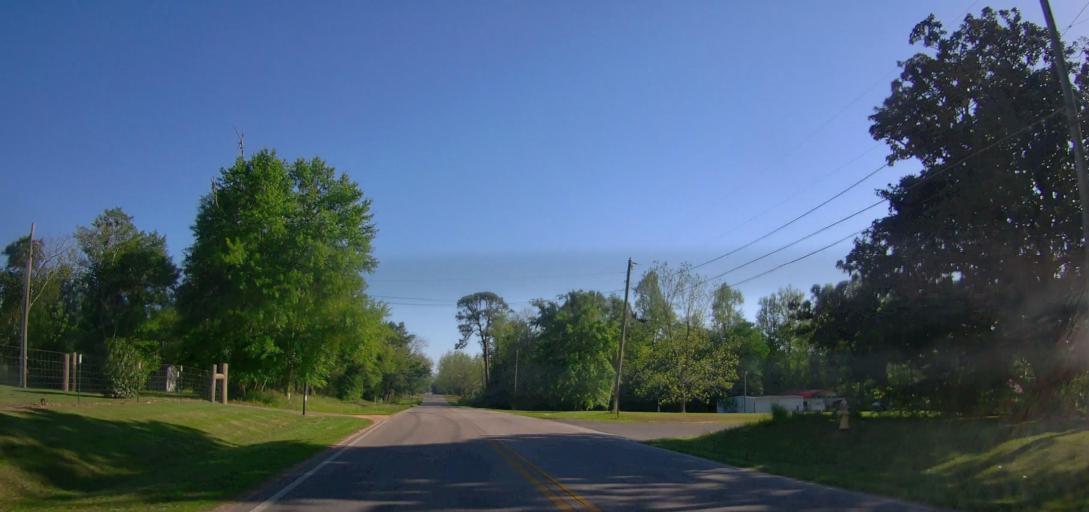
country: US
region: Georgia
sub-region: Ben Hill County
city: Fitzgerald
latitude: 31.7251
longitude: -83.2354
